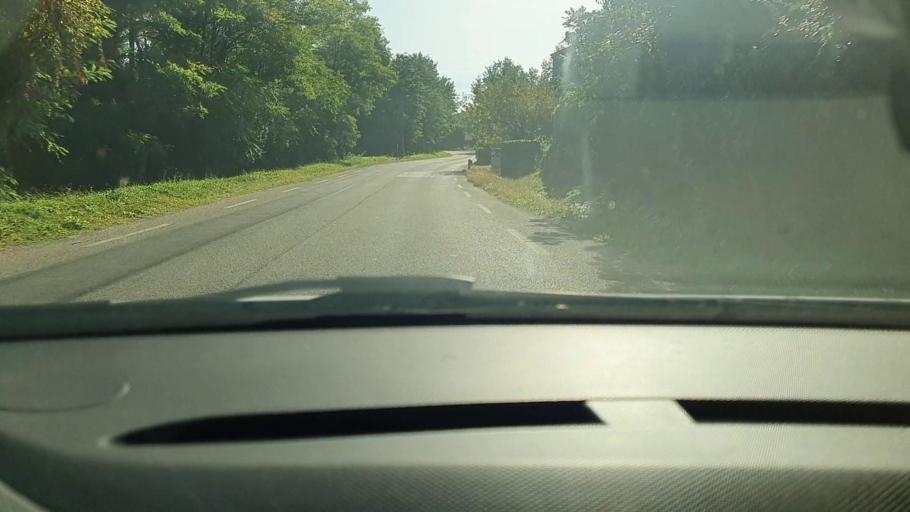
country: FR
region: Languedoc-Roussillon
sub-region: Departement du Gard
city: Besseges
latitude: 44.2837
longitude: 4.1122
